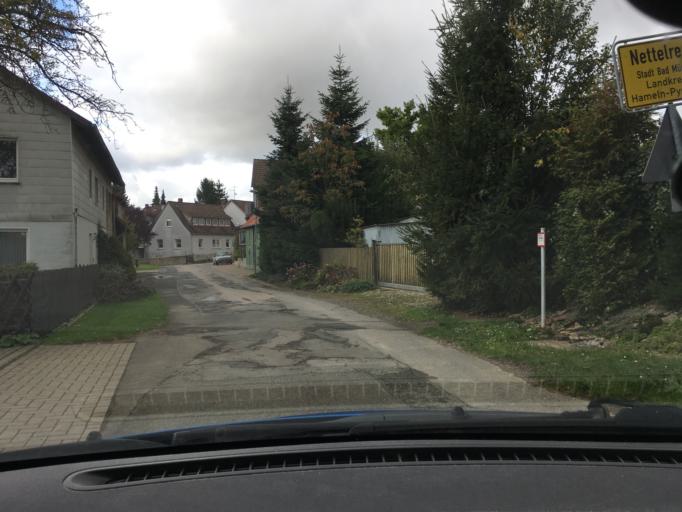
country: DE
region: Lower Saxony
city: Bad Munder am Deister
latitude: 52.2192
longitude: 9.4604
